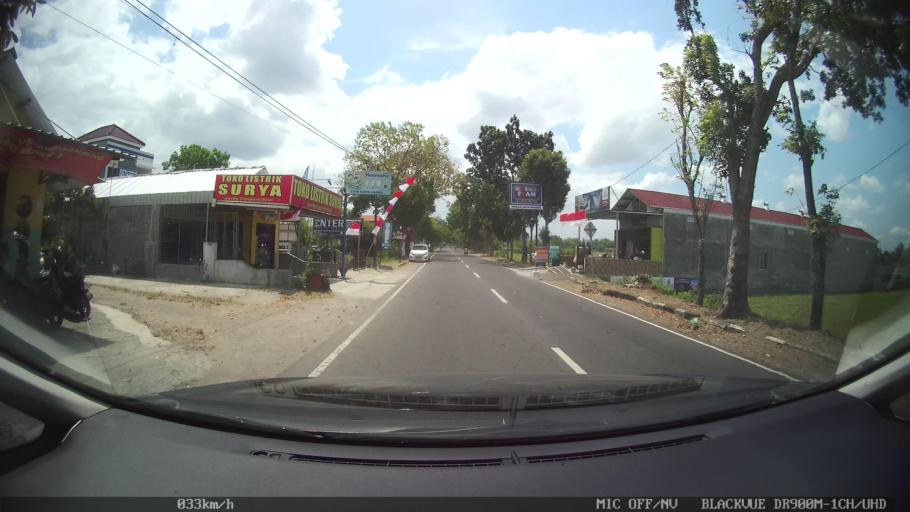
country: ID
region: Daerah Istimewa Yogyakarta
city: Bantul
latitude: -7.8901
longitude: 110.3334
